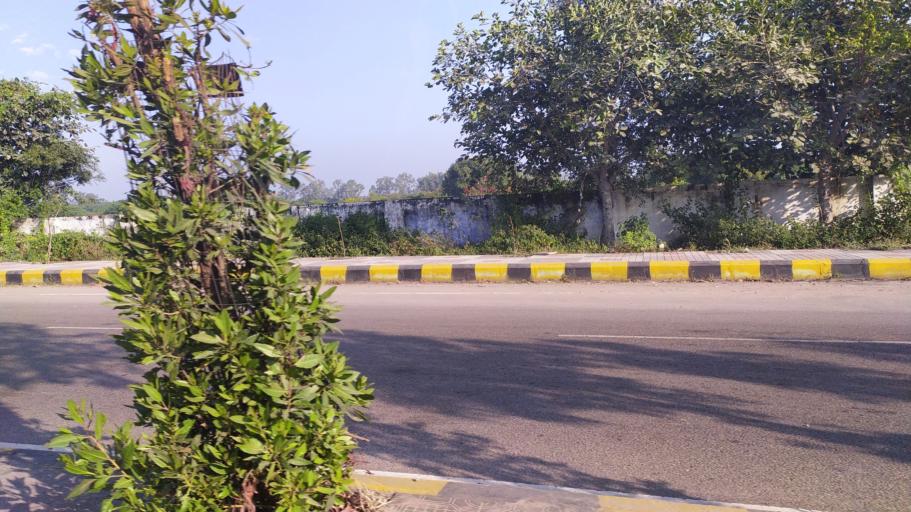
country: IN
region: Telangana
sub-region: Hyderabad
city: Hyderabad
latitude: 17.3197
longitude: 78.3915
